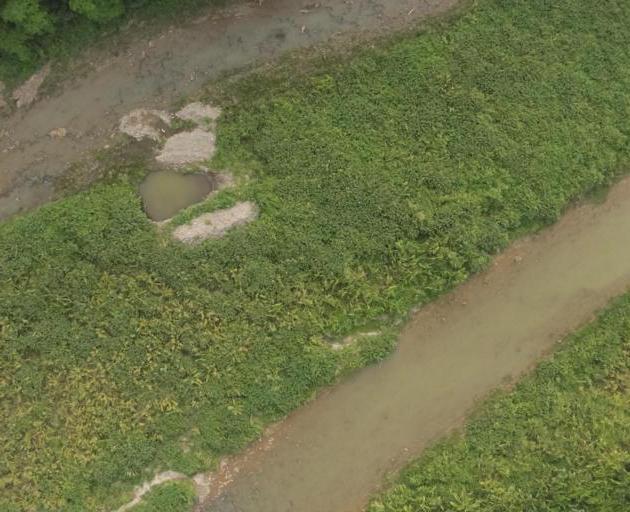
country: BO
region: La Paz
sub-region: Provincia Larecaja
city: Guanay
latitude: -15.7716
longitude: -67.6627
